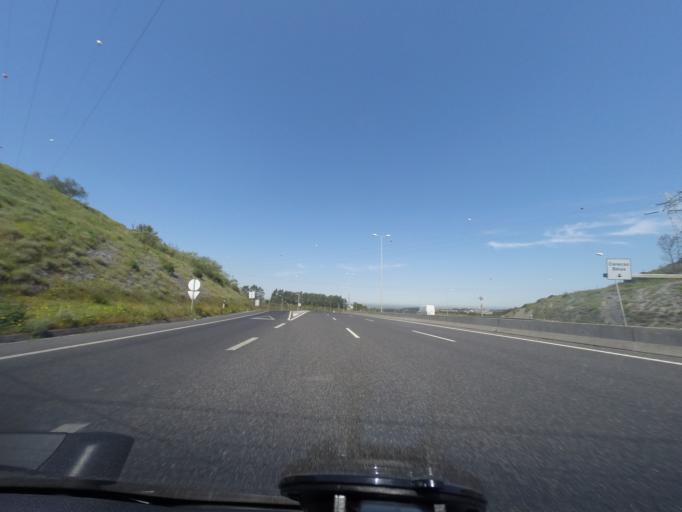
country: PT
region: Lisbon
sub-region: Odivelas
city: Famoes
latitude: 38.7849
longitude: -9.2324
